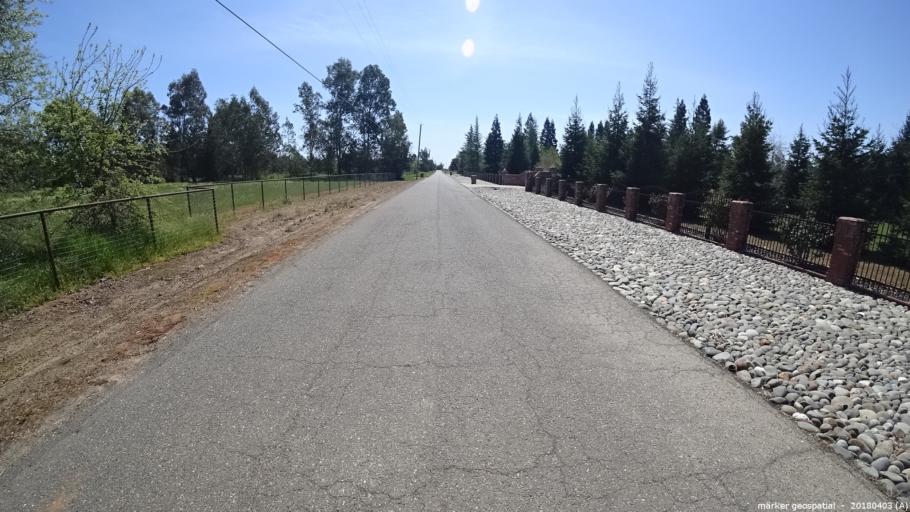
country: US
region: California
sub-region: Sacramento County
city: Wilton
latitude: 38.3867
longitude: -121.2468
